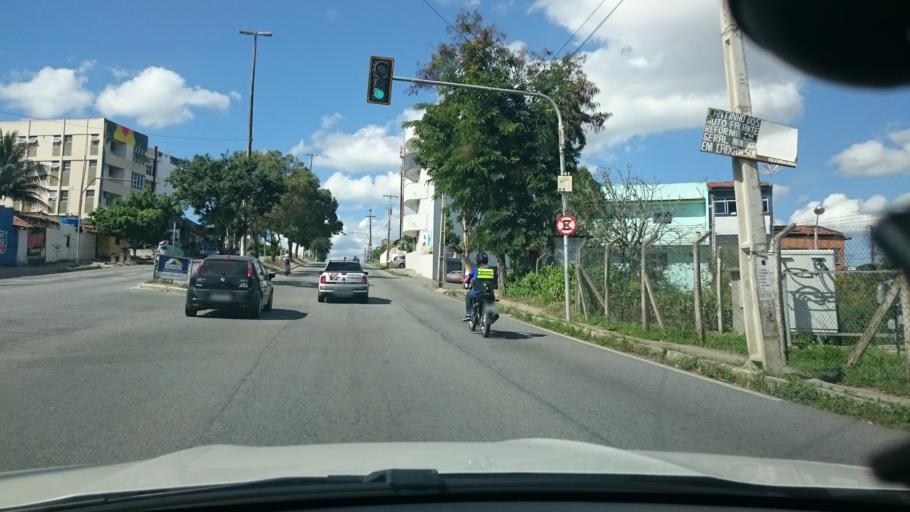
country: BR
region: Paraiba
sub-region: Campina Grande
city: Campina Grande
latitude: -7.2257
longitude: -35.8970
